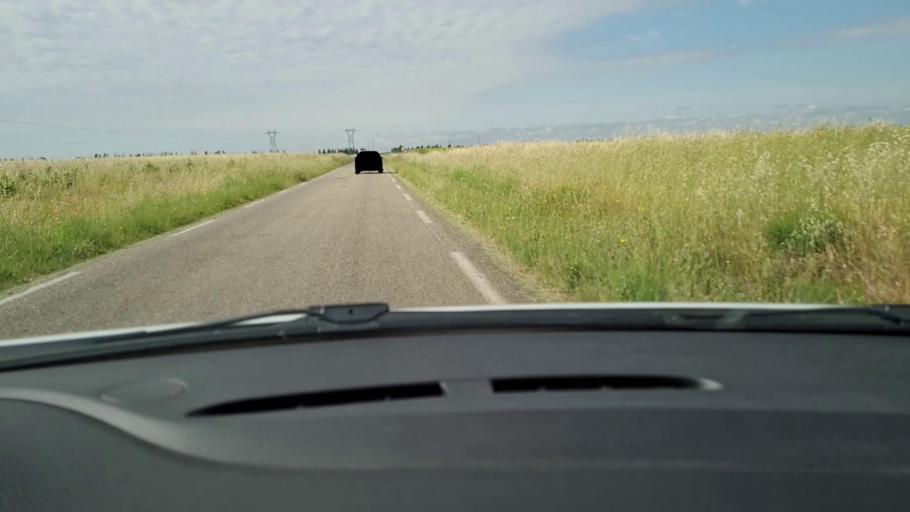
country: FR
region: Languedoc-Roussillon
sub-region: Departement du Gard
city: Bellegarde
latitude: 43.7807
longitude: 4.5228
